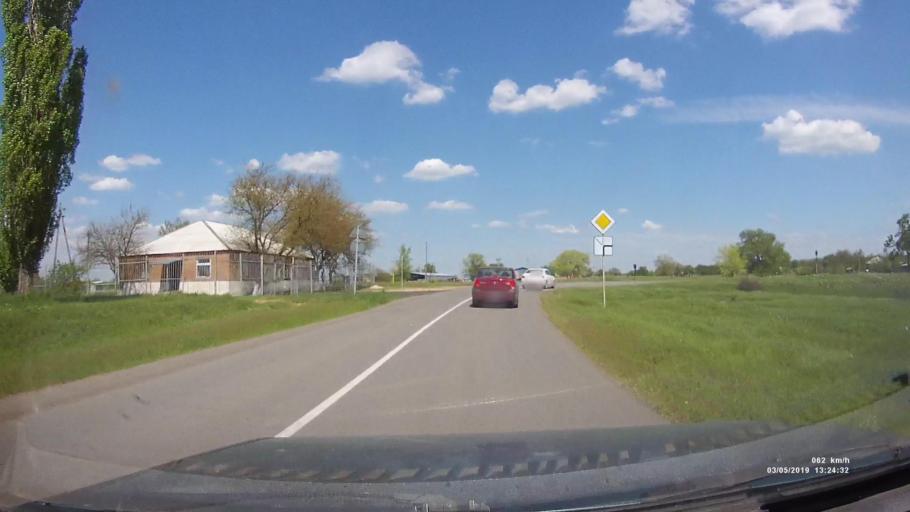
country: RU
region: Rostov
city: Semikarakorsk
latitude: 47.5658
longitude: 40.7969
